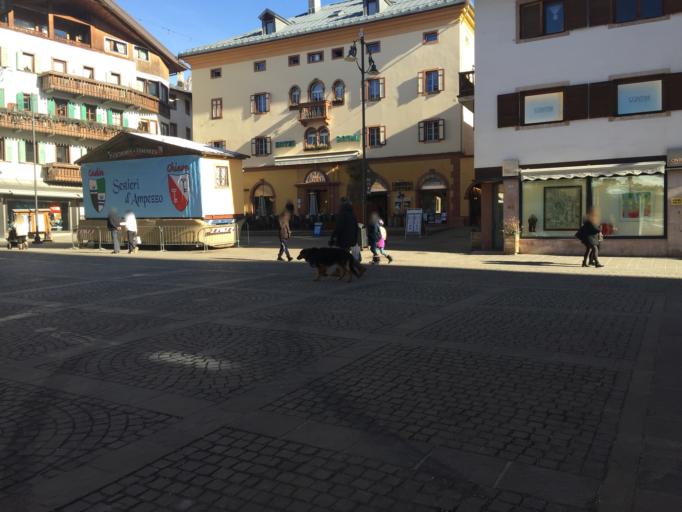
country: IT
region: Veneto
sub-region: Provincia di Belluno
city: Cortina d'Ampezzo
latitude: 46.5380
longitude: 12.1360
